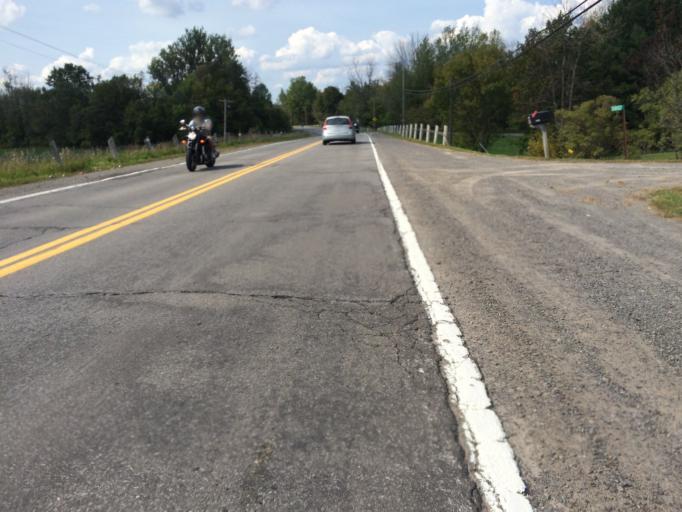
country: CA
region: Ontario
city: Bells Corners
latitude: 45.2055
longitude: -75.6534
